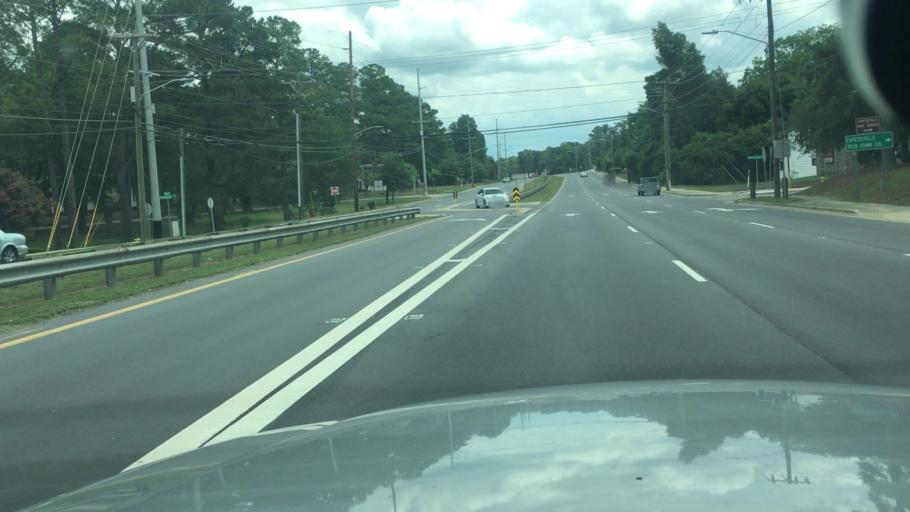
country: US
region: North Carolina
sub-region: Cumberland County
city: Fayetteville
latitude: 35.0714
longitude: -78.9211
